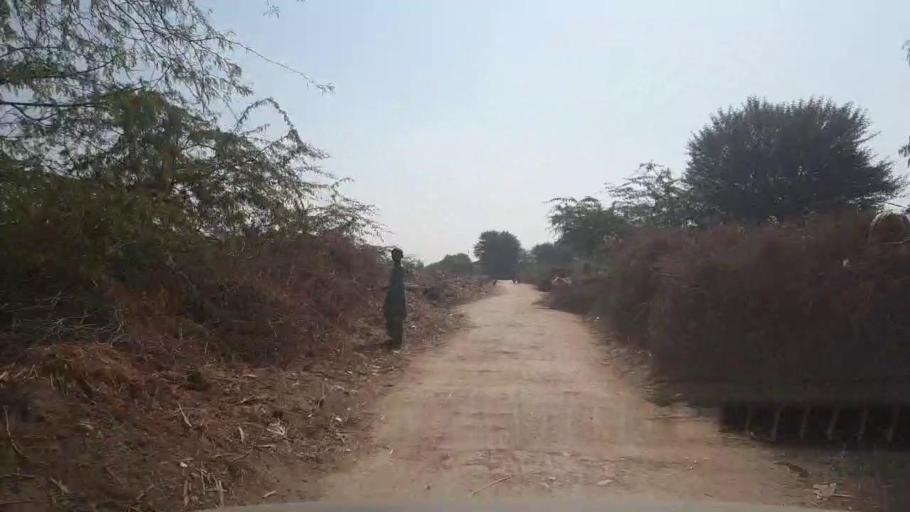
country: PK
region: Sindh
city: Chambar
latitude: 25.2608
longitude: 68.8332
